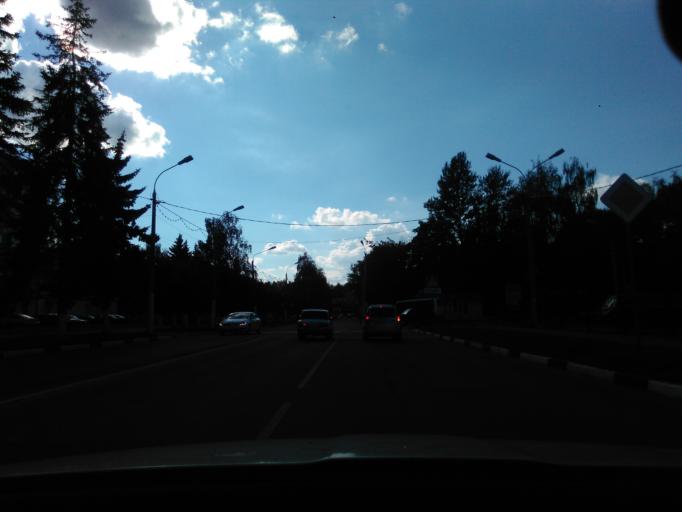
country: RU
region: Moskovskaya
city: Klin
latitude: 56.3193
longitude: 36.7284
